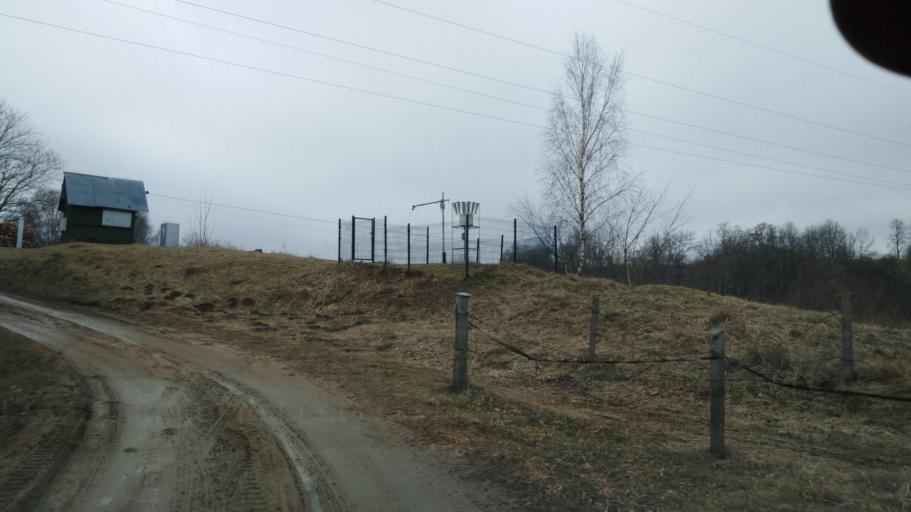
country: LV
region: Kuldigas Rajons
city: Kuldiga
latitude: 56.9869
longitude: 21.9612
